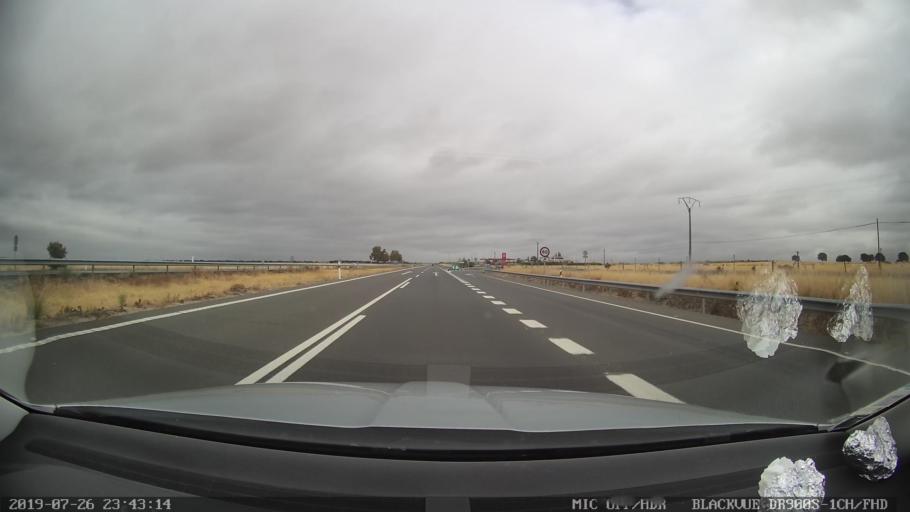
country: ES
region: Extremadura
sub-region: Provincia de Caceres
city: Trujillo
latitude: 39.5217
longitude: -5.8343
